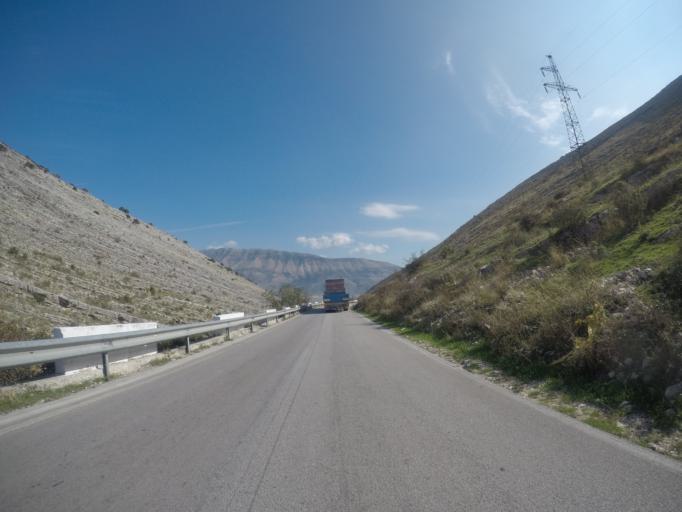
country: AL
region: Gjirokaster
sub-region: Rrethi i Gjirokastres
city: Libohove
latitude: 39.9442
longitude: 20.2322
